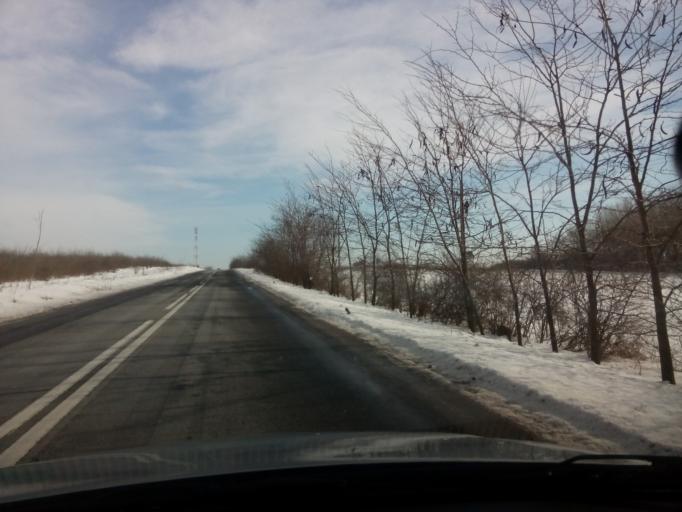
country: RO
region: Calarasi
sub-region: Comuna Budesti
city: Budesti
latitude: 44.2320
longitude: 26.4811
